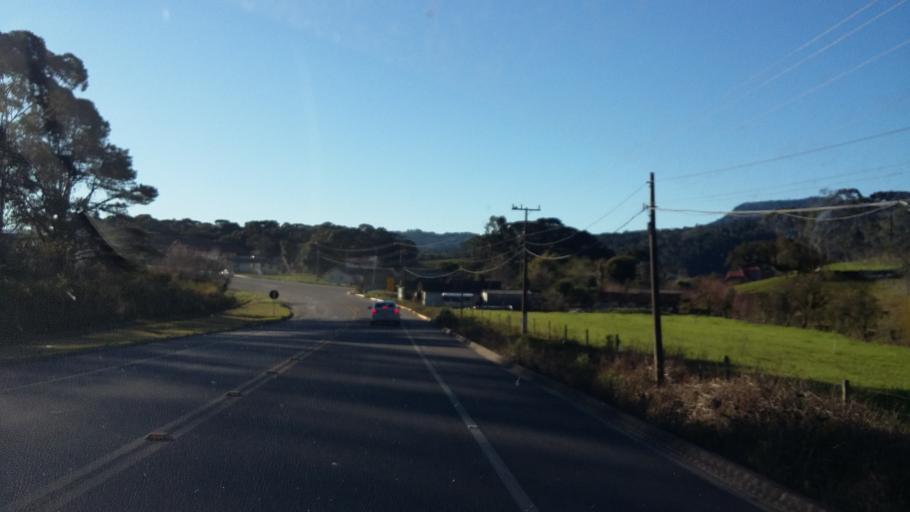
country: BR
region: Santa Catarina
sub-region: Lauro Muller
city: Lauro Muller
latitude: -28.0025
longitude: -49.5468
